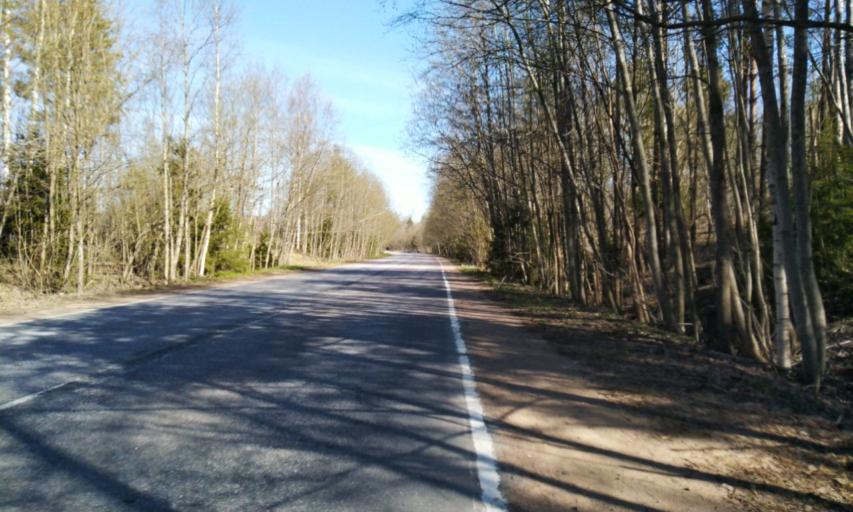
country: RU
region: Leningrad
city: Garbolovo
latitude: 60.3927
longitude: 30.4777
